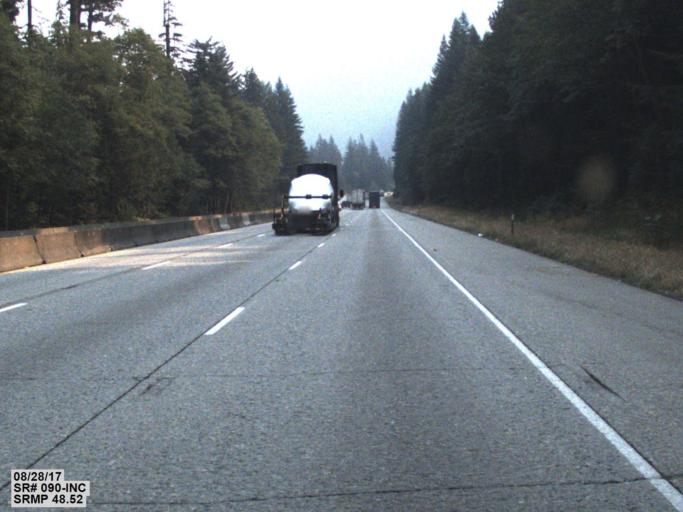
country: US
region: Washington
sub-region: King County
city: Tanner
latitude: 47.3940
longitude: -121.4639
